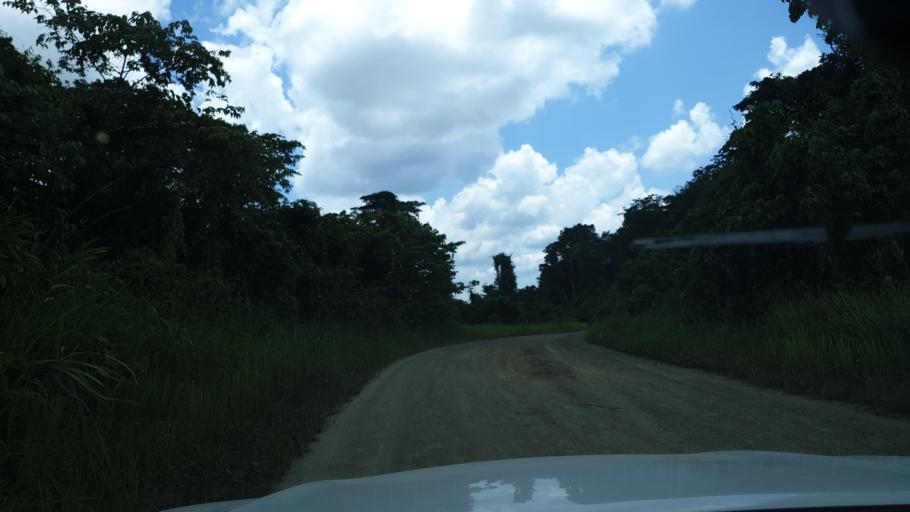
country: PG
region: East Sepik
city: Angoram
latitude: -3.8240
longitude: 143.8560
